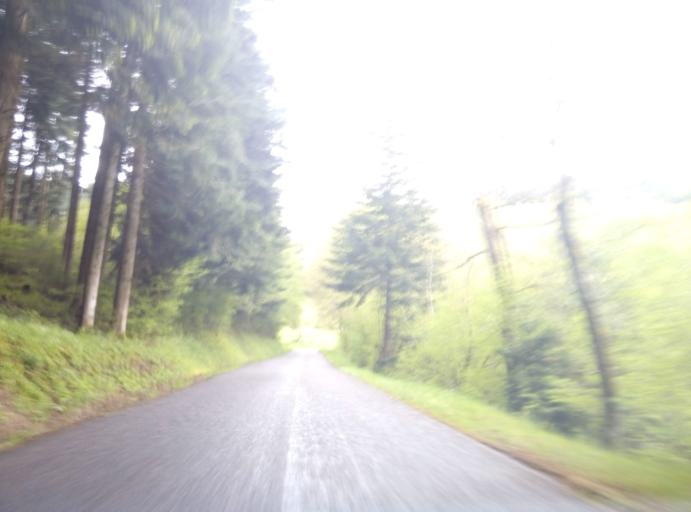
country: FR
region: Rhone-Alpes
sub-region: Departement du Rhone
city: Cublize
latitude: 45.9701
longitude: 4.4183
